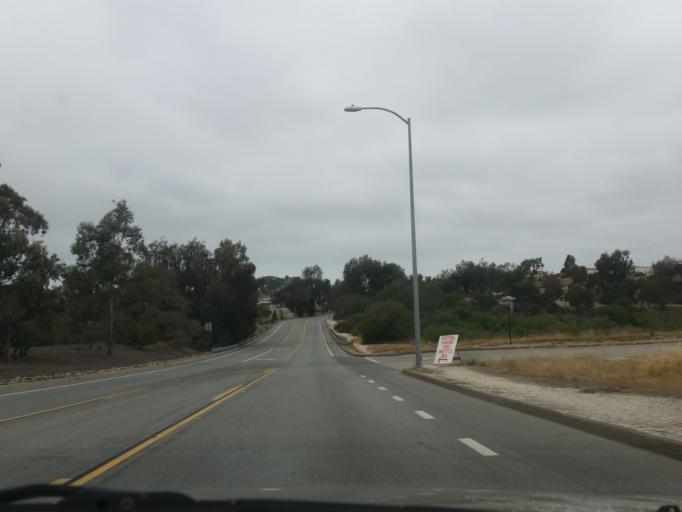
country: US
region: California
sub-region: San Luis Obispo County
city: Arroyo Grande
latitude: 35.1231
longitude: -120.5870
